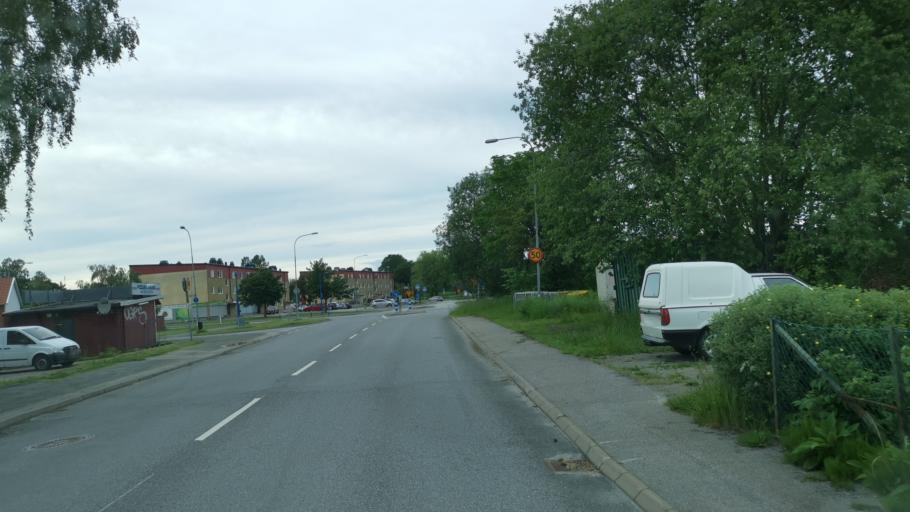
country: SE
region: Vaestra Goetaland
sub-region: Vanersborgs Kommun
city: Vargon
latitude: 58.3627
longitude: 12.3561
